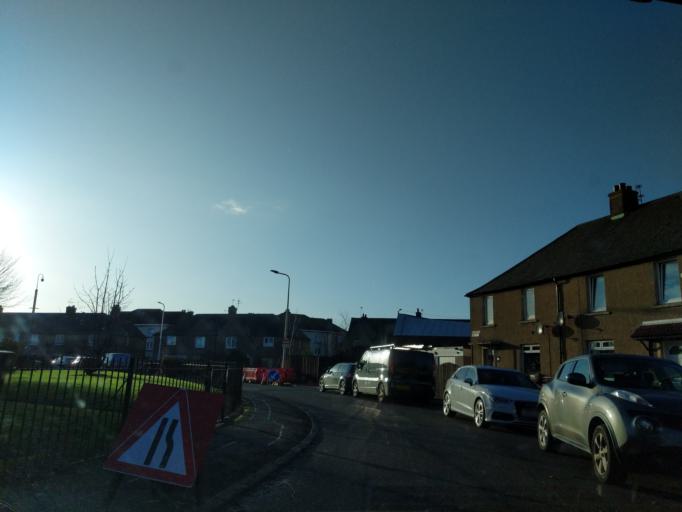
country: GB
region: Scotland
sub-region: Edinburgh
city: Colinton
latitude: 55.9288
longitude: -3.2770
